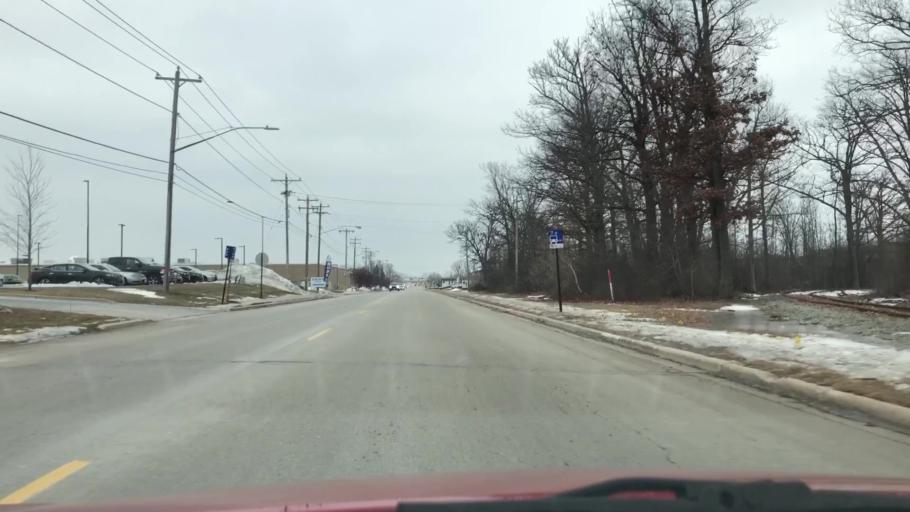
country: US
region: Wisconsin
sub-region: Brown County
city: Ashwaubenon
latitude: 44.4709
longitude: -88.0724
